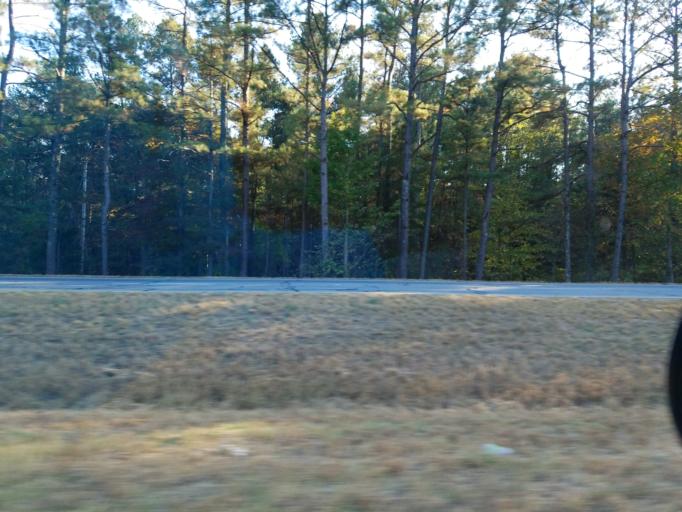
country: US
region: Georgia
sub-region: Bartow County
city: Euharlee
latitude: 34.2243
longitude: -84.8957
